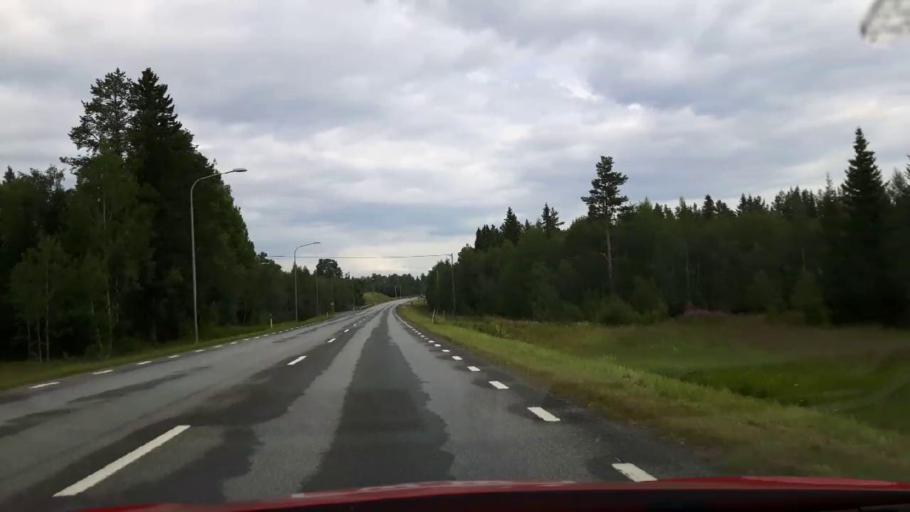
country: SE
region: Jaemtland
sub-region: Stroemsunds Kommun
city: Stroemsund
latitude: 63.6778
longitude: 15.3981
